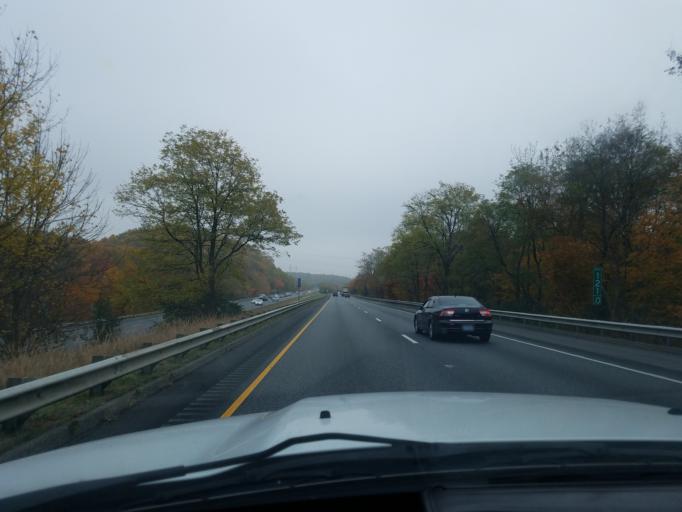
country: US
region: Indiana
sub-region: Floyd County
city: New Albany
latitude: 38.3012
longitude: -85.8651
